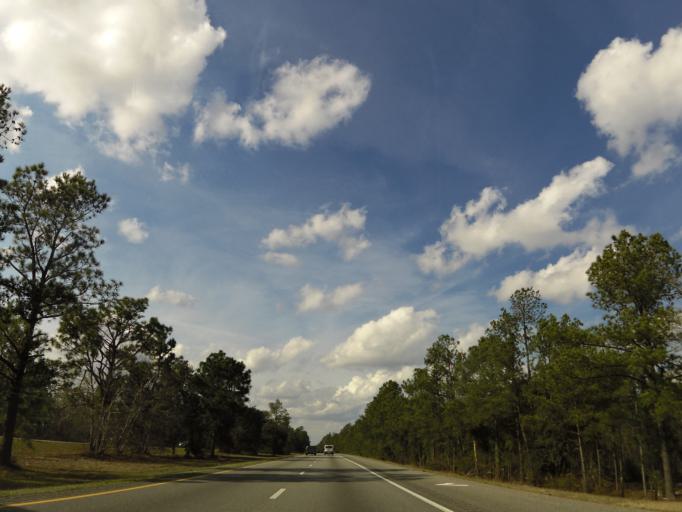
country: US
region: South Carolina
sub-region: Dorchester County
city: Ridgeville
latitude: 33.1701
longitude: -80.3643
